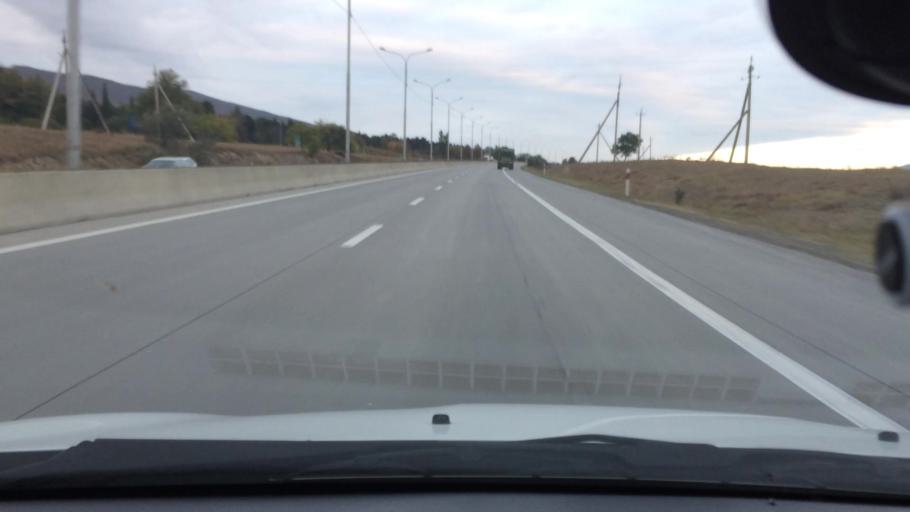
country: GE
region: Shida Kartli
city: Kaspi
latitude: 41.9337
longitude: 44.5191
